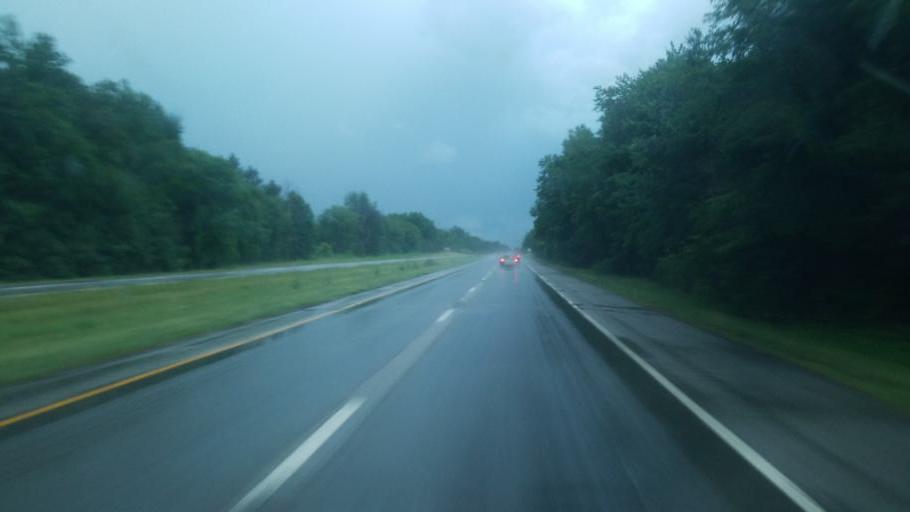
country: US
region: Ohio
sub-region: Wayne County
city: Doylestown
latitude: 40.9568
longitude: -81.6589
